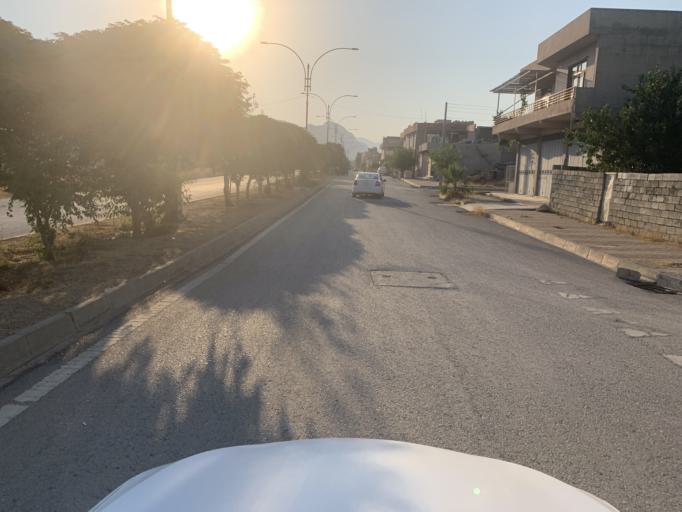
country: IQ
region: As Sulaymaniyah
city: Raniye
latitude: 36.2376
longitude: 44.8813
